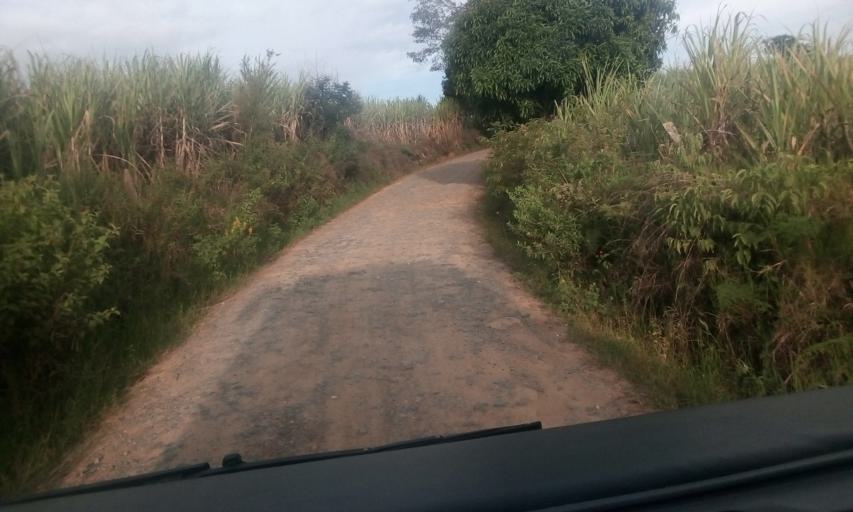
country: CO
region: Boyaca
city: Santana
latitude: 6.0222
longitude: -73.5147
